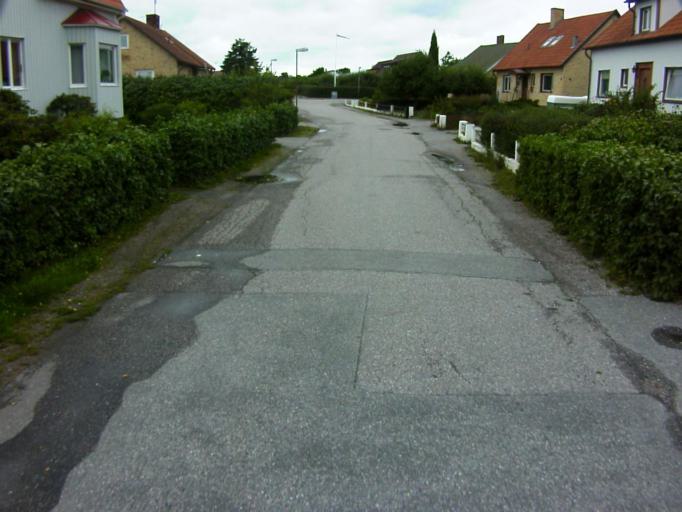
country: SE
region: Soedermanland
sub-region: Eskilstuna Kommun
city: Eskilstuna
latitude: 59.3770
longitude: 16.4830
